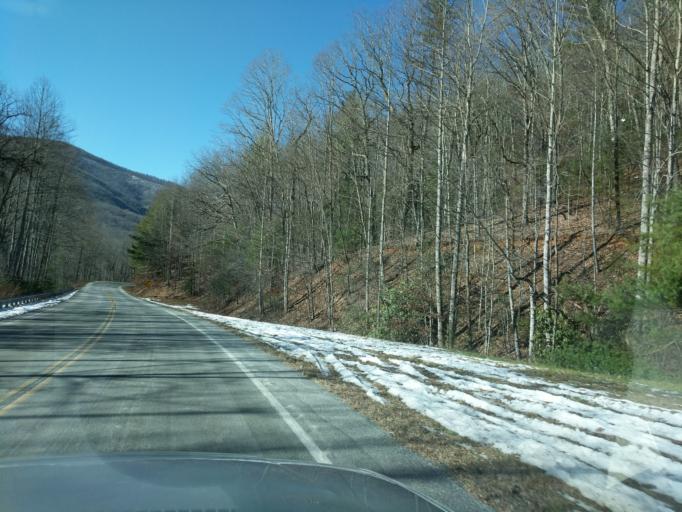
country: US
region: Georgia
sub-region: Towns County
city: Hiawassee
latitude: 34.8951
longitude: -83.6021
